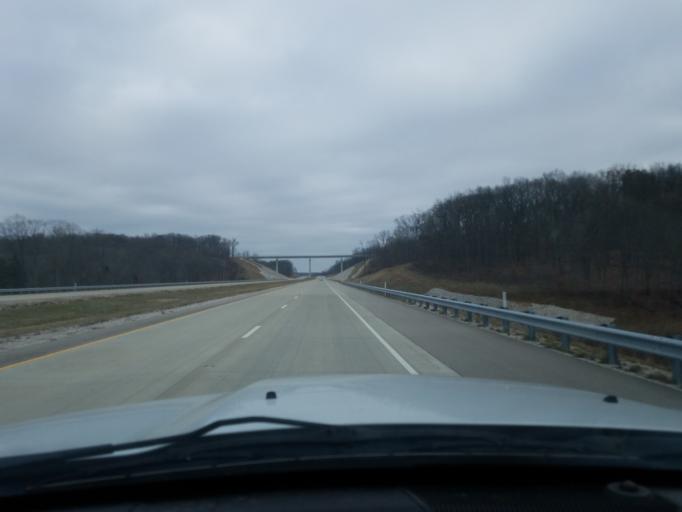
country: US
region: Indiana
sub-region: Monroe County
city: Bloomington
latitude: 39.0729
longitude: -86.6354
